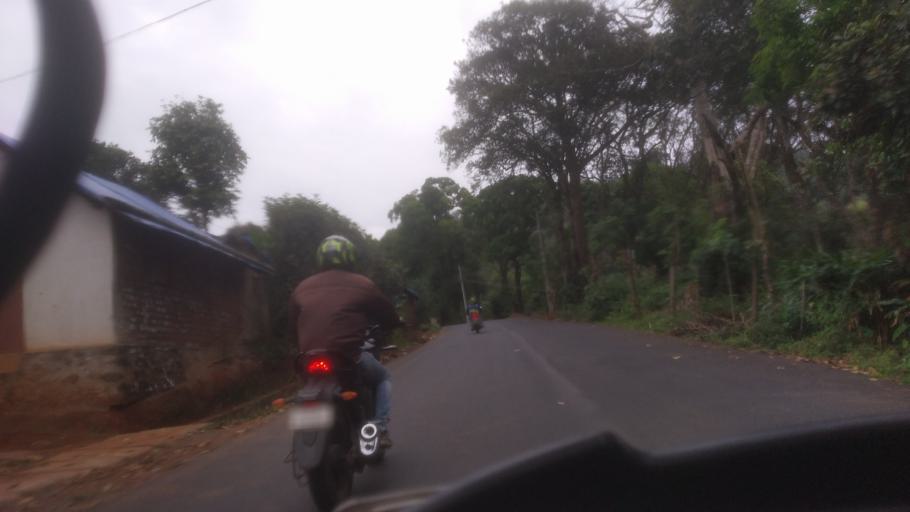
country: IN
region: Tamil Nadu
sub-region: Theni
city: Kombai
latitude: 9.8926
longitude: 77.1434
